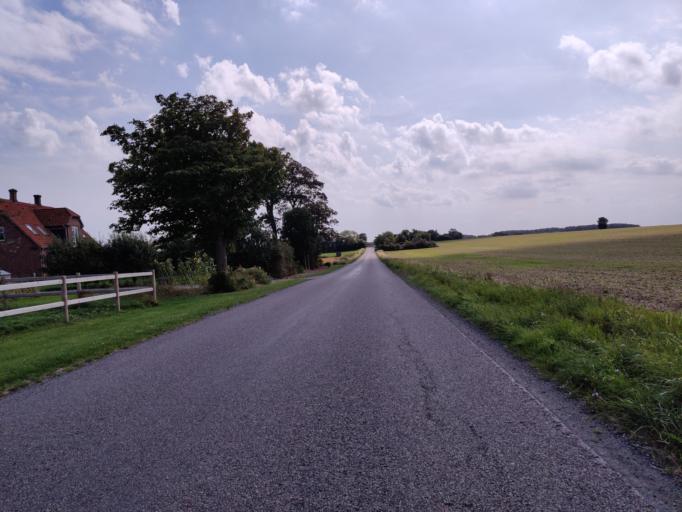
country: DK
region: Zealand
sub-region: Guldborgsund Kommune
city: Nykobing Falster
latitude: 54.6632
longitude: 11.8903
